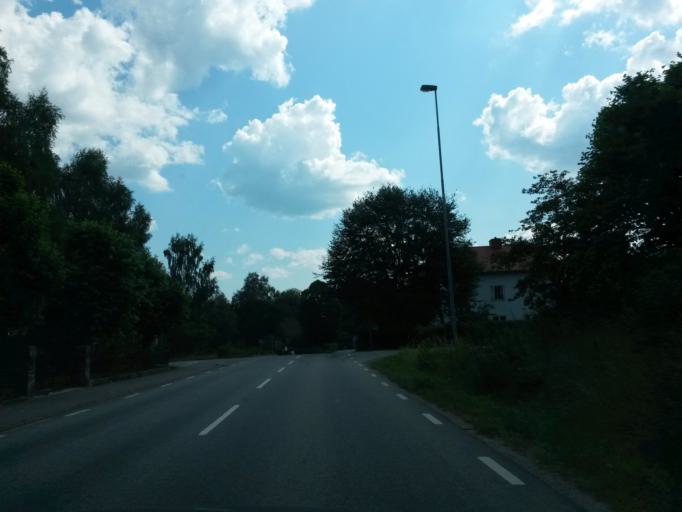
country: SE
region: Vaestra Goetaland
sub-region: Herrljunga Kommun
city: Herrljunga
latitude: 58.0789
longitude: 13.0111
